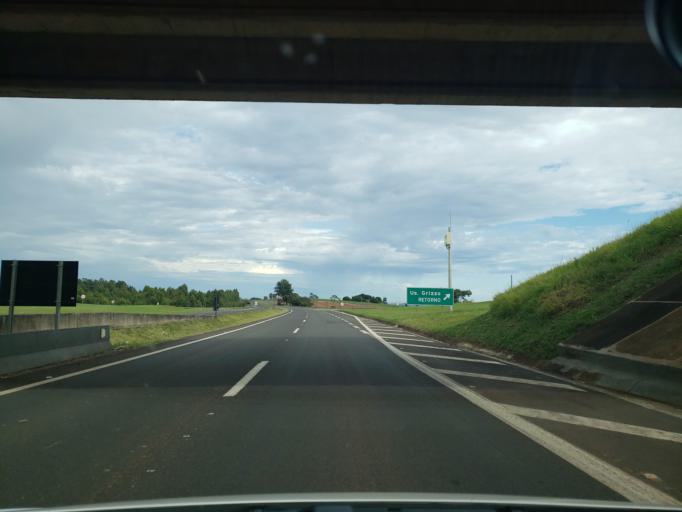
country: BR
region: Sao Paulo
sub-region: Dois Corregos
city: Dois Corregos
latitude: -22.2656
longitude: -48.4425
